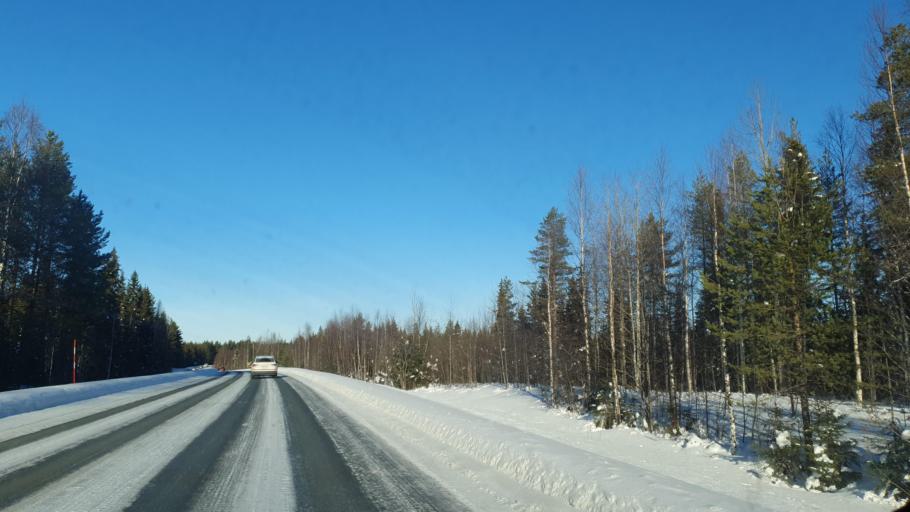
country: FI
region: Lapland
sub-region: Torniolaakso
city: Pello
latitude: 66.7092
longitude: 23.9046
